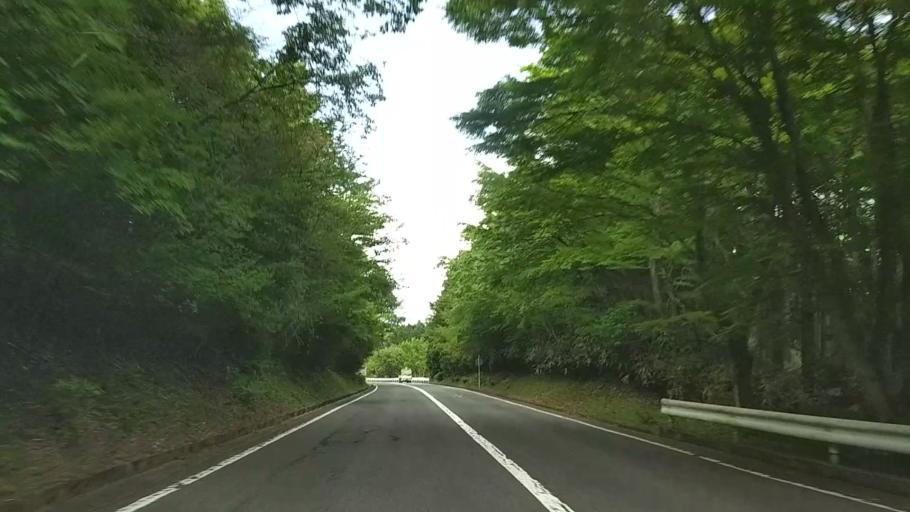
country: JP
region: Kanagawa
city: Yugawara
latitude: 35.2135
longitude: 139.0980
